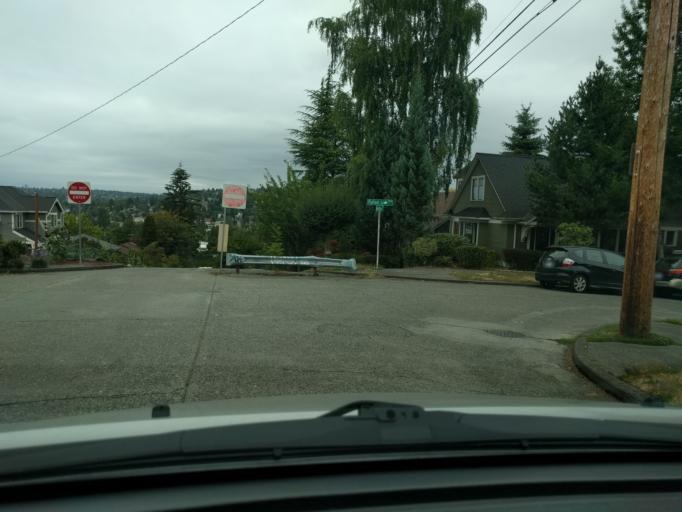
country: US
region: Washington
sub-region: King County
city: Seattle
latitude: 47.6457
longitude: -122.3569
